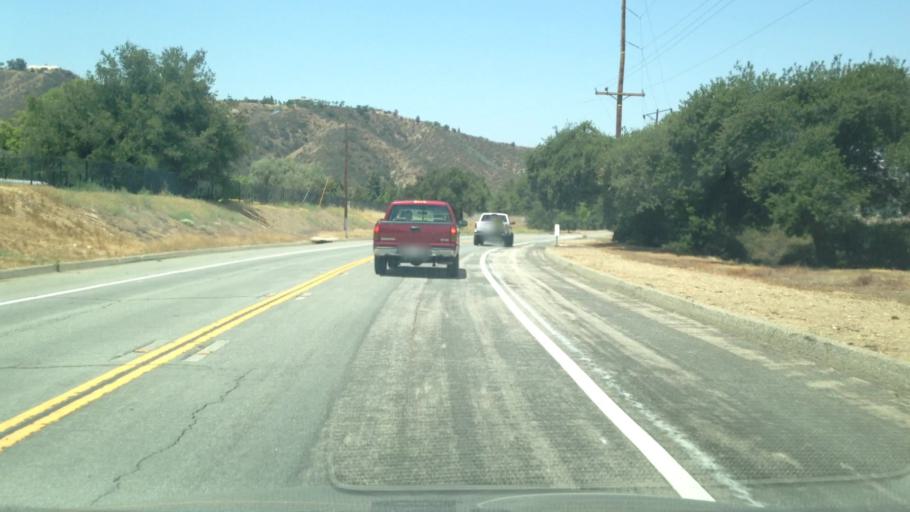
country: US
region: California
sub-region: Riverside County
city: Cherry Valley
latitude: 34.0086
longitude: -116.9840
